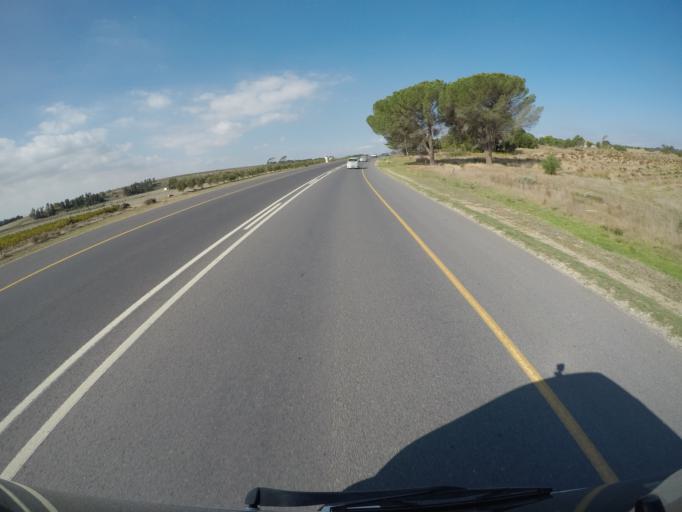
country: ZA
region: Western Cape
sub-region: City of Cape Town
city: Kraaifontein
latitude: -33.8777
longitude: 18.7690
